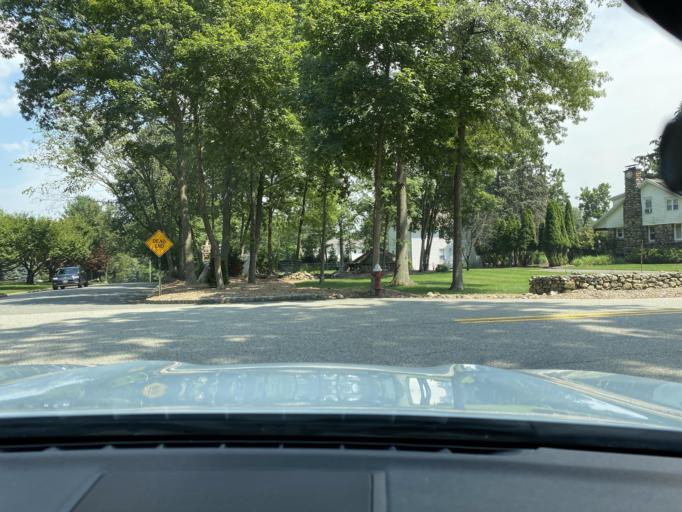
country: US
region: New York
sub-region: Rockland County
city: Airmont
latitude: 41.0883
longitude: -74.1126
